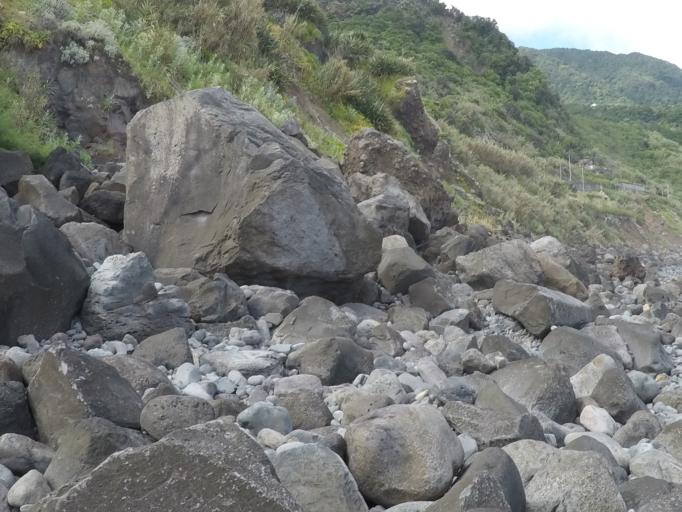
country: PT
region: Madeira
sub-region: Sao Vicente
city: Sao Vicente
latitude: 32.8234
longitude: -17.0012
